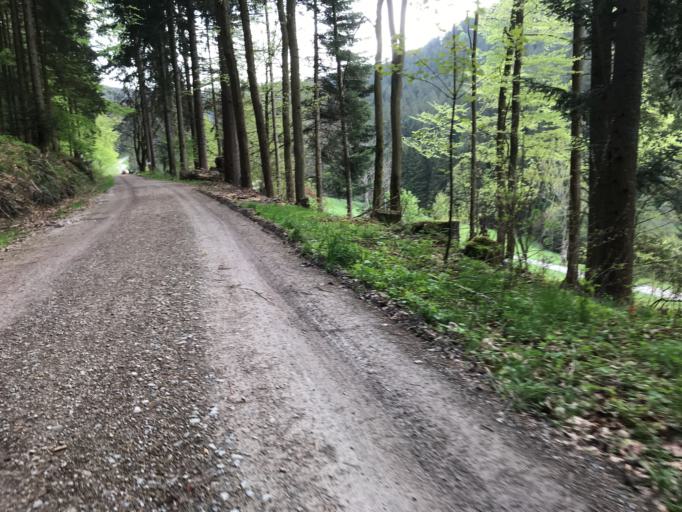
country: DE
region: Baden-Wuerttemberg
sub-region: Karlsruhe Region
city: Baiersbronn
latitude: 48.4919
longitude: 8.3603
